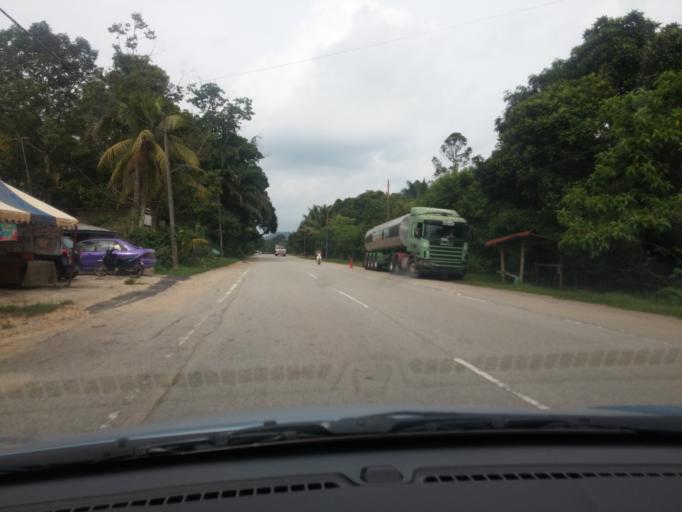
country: MY
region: Pahang
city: Kuantan
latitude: 3.8839
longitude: 103.1616
